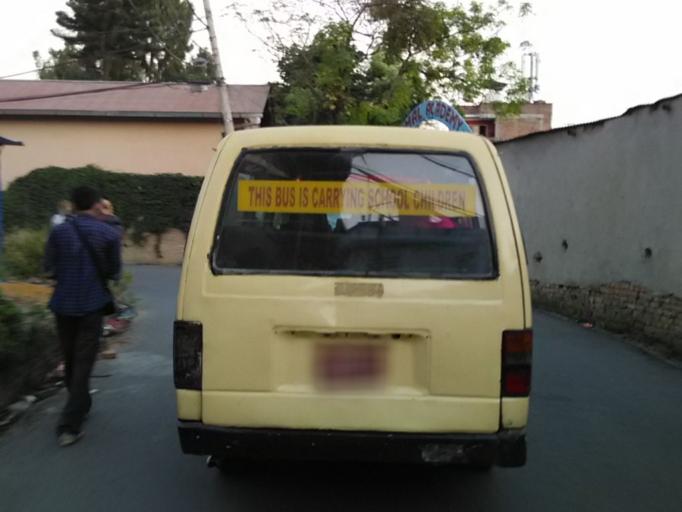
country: NP
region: Central Region
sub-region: Bagmati Zone
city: Kathmandu
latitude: 27.7271
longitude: 85.3341
